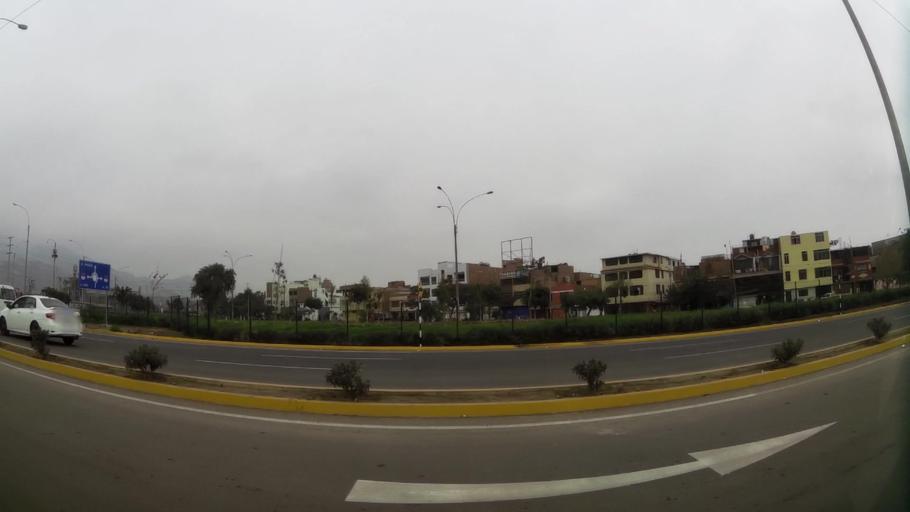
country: PE
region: Lima
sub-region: Lima
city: Independencia
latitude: -11.9778
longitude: -77.0676
